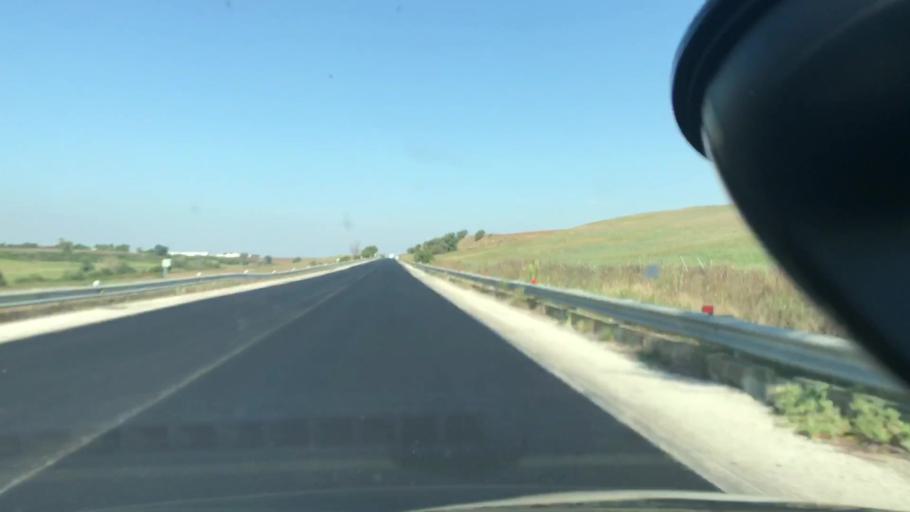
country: IT
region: Apulia
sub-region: Provincia di Barletta - Andria - Trani
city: Spinazzola
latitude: 40.9028
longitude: 16.1175
